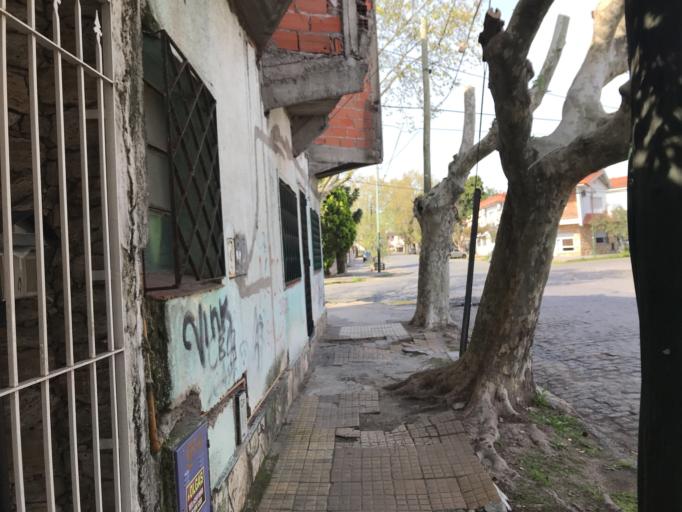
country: AR
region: Buenos Aires
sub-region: Partido de Lomas de Zamora
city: Lomas de Zamora
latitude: -34.7709
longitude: -58.4001
